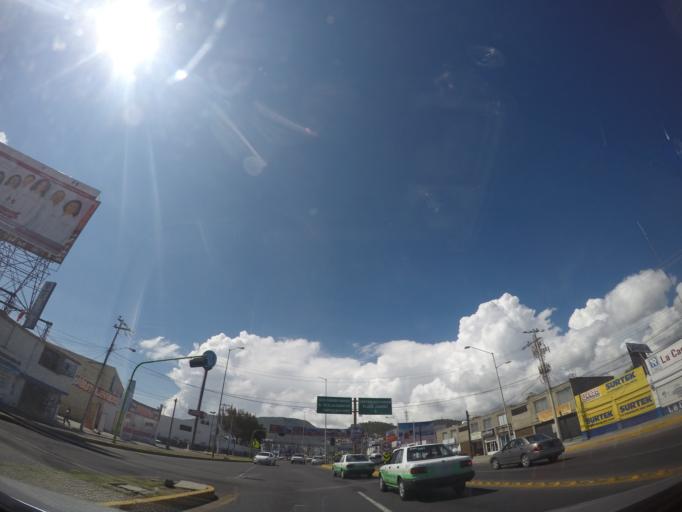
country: MX
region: Hidalgo
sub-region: Mineral de la Reforma
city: Unidad Minera 11 de Julio
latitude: 20.1098
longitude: -98.7220
